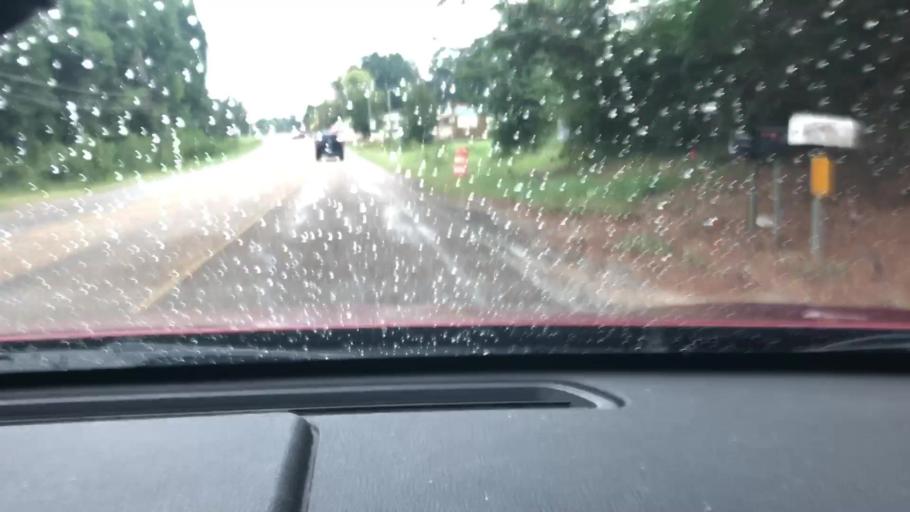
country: US
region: Texas
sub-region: Bowie County
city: Wake Village
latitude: 33.4428
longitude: -94.1133
